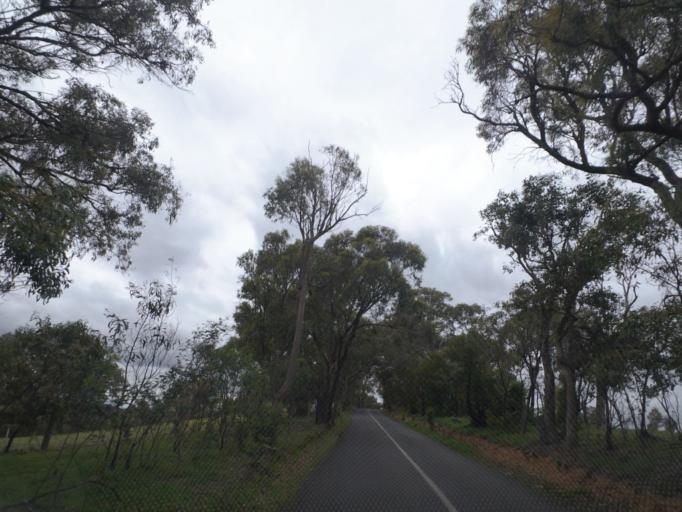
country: AU
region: Victoria
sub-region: Nillumbik
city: Hurstbridge
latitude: -37.6571
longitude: 145.2462
